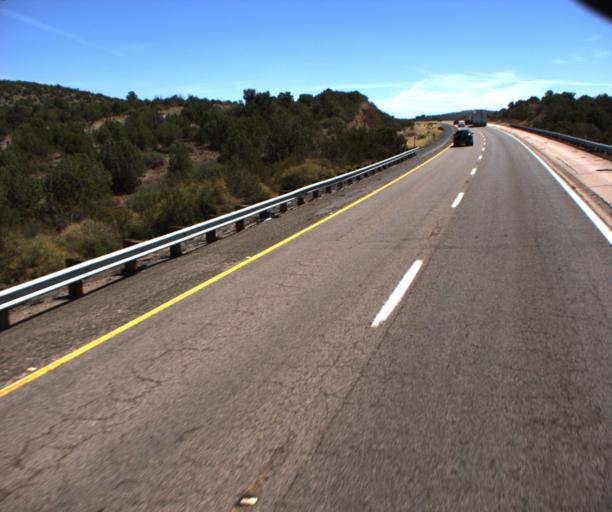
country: US
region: Arizona
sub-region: Mohave County
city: Peach Springs
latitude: 35.1896
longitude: -113.3159
